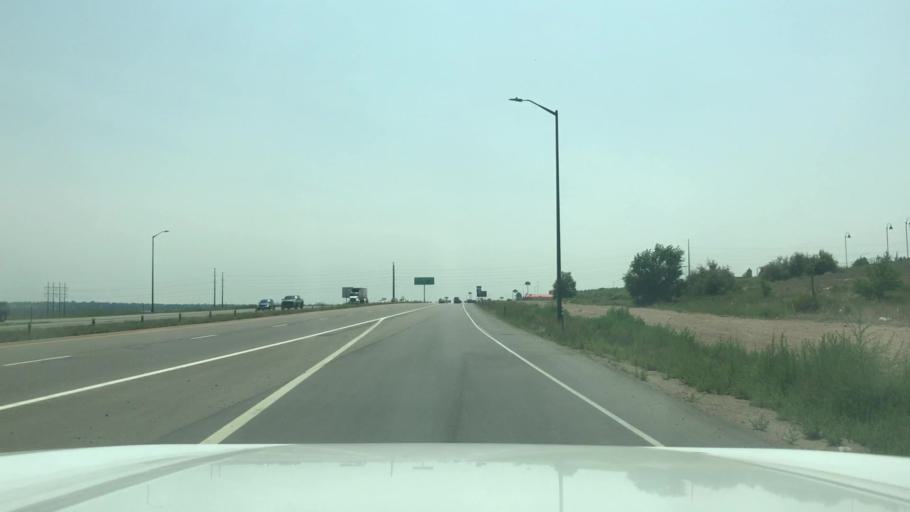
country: US
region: Colorado
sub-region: Pueblo County
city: Pueblo
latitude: 38.3355
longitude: -104.6192
